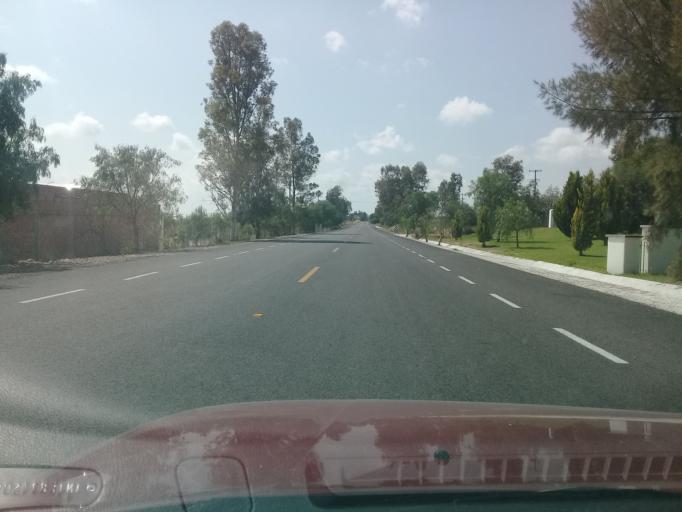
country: MX
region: Aguascalientes
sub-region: Aguascalientes
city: Penuelas (El Cienegal)
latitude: 21.7267
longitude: -102.3613
